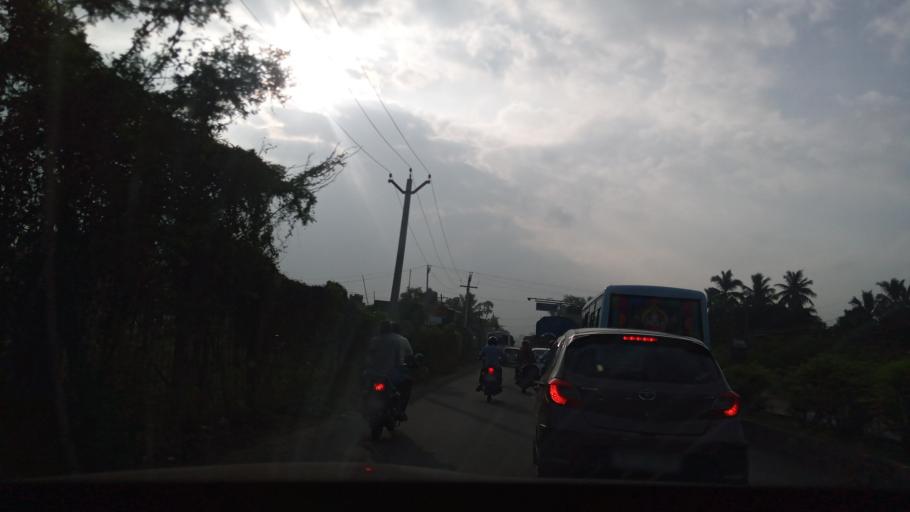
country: IN
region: Tamil Nadu
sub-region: Kancheepuram
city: Vengavasal
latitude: 12.8589
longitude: 80.1328
